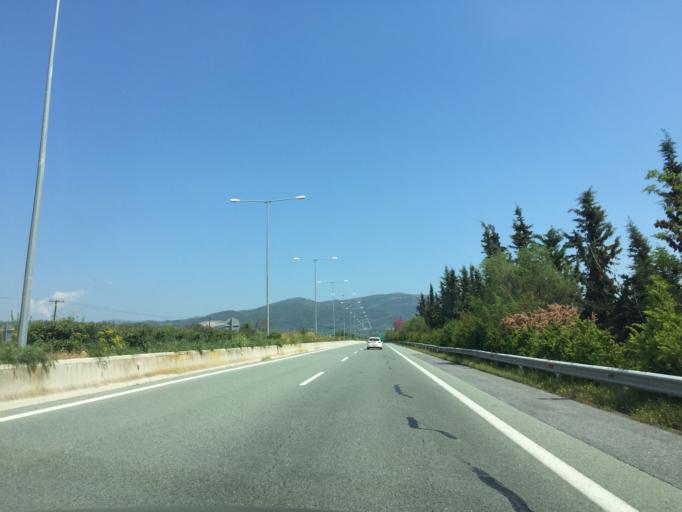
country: GR
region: Central Greece
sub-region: Nomos Fthiotidos
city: Pelasgia
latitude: 38.9335
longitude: 22.8645
